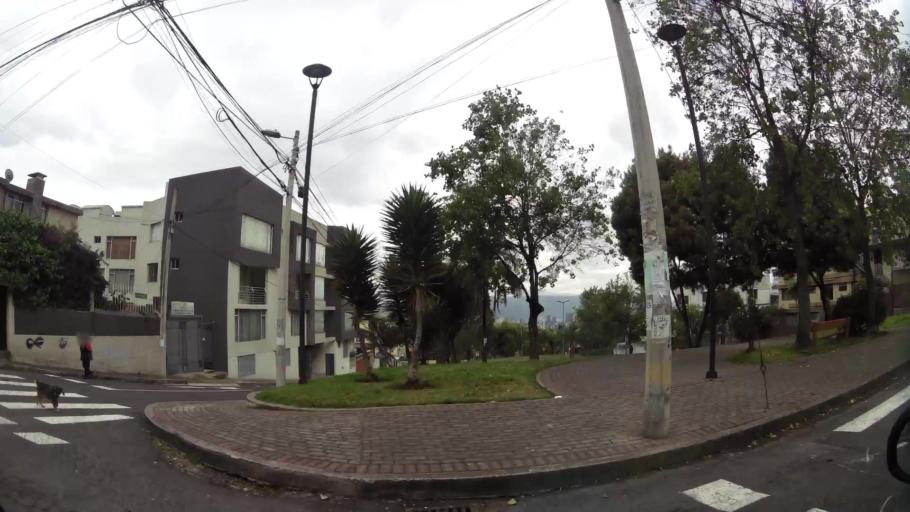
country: EC
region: Pichincha
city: Quito
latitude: -0.1927
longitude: -78.5090
